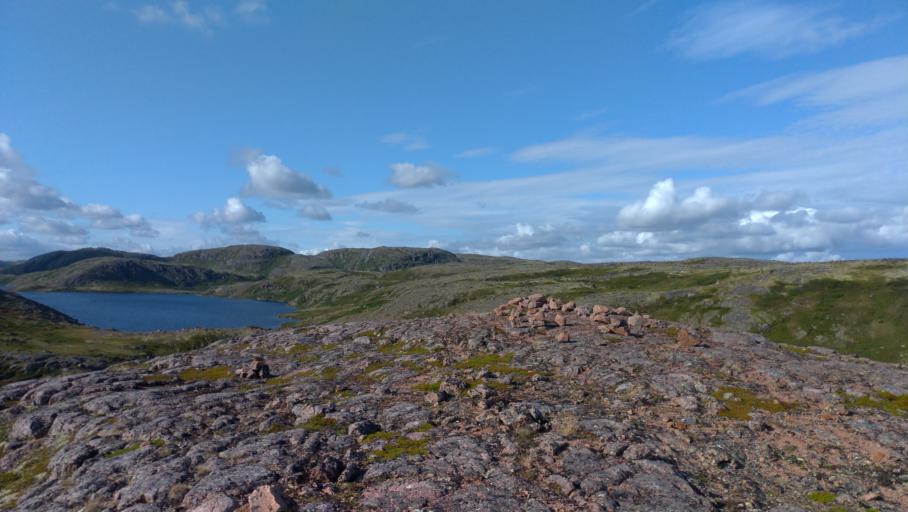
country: RU
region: Murmansk
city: Teriberka
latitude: 69.2038
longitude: 35.0635
